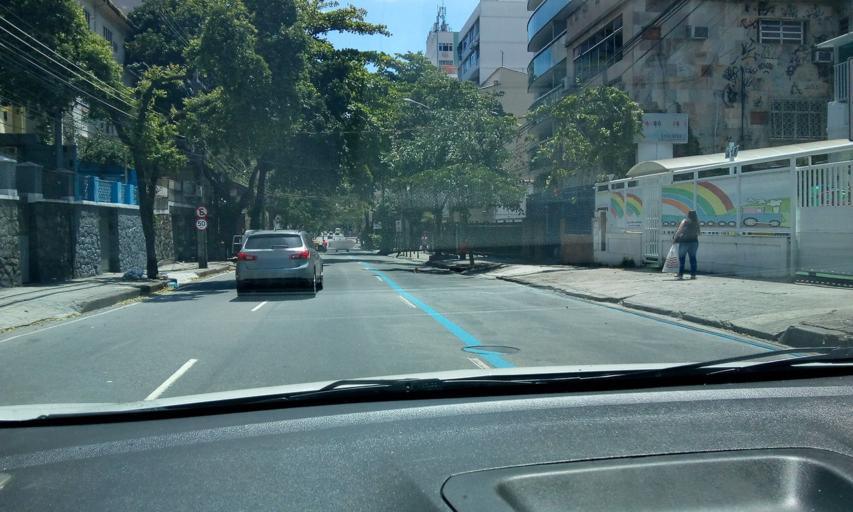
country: BR
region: Rio de Janeiro
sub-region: Rio De Janeiro
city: Rio de Janeiro
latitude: -22.9175
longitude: -43.2154
